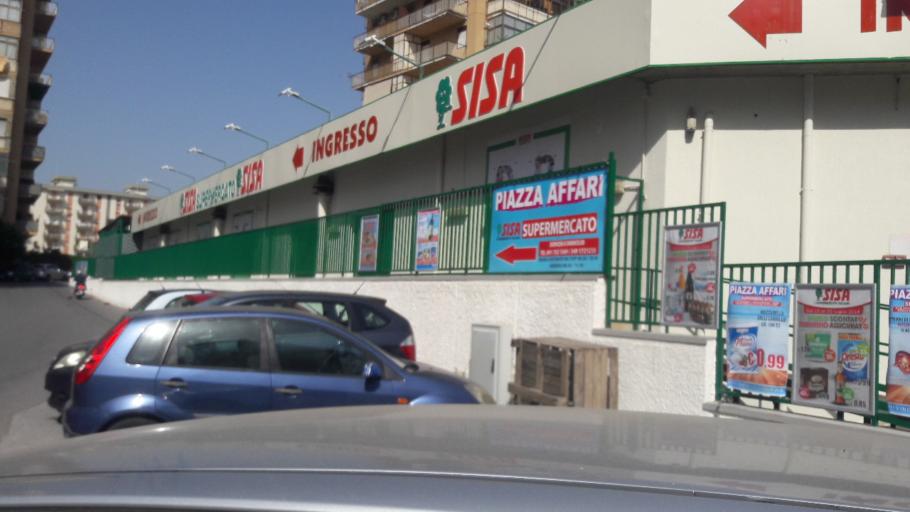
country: IT
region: Sicily
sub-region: Palermo
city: Ciaculli
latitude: 38.0925
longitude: 13.3650
